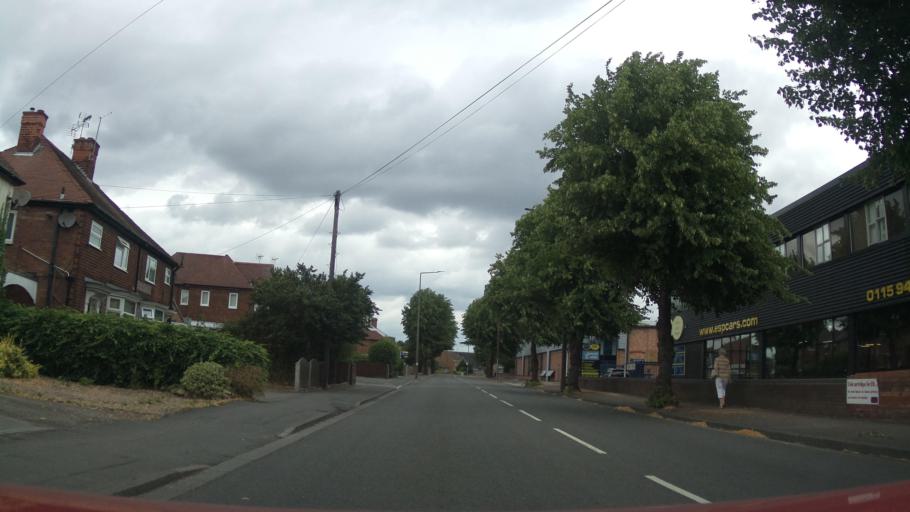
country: GB
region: England
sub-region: Derbyshire
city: Long Eaton
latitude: 52.8881
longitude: -1.2881
